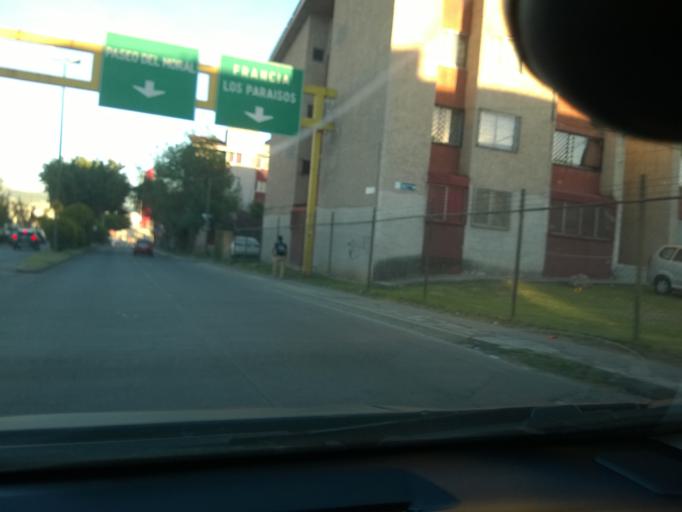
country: MX
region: Guanajuato
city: Leon
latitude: 21.1439
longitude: -101.6946
